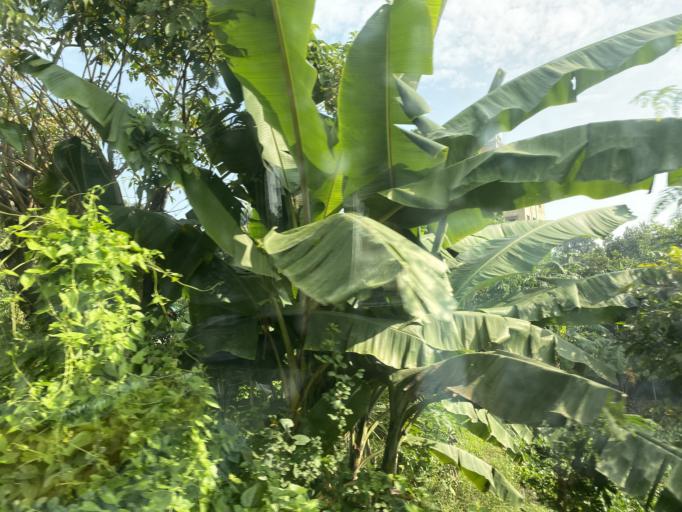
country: BD
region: Dhaka
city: Bhairab Bazar
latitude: 23.9664
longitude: 91.1163
